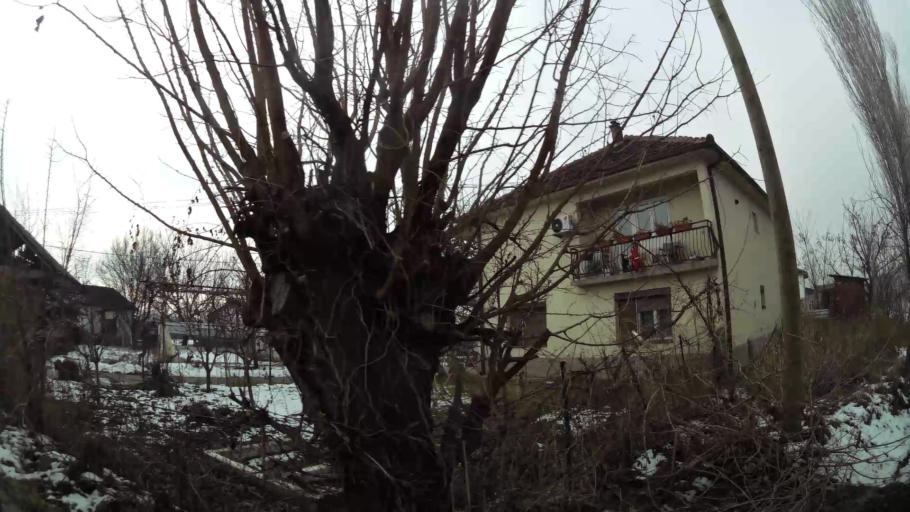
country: MK
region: Ilinden
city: Ilinden
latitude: 41.9910
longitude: 21.5761
